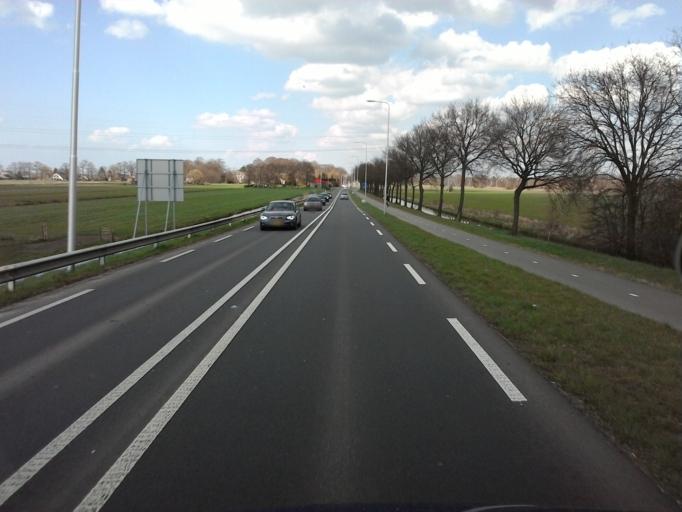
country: NL
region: Utrecht
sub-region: Gemeente De Bilt
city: De Bilt
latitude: 52.1443
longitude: 5.1565
